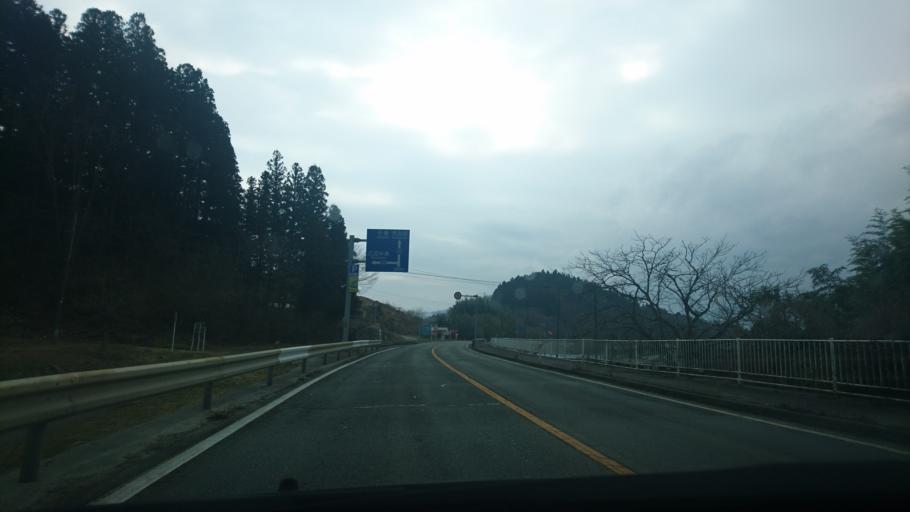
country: JP
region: Iwate
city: Ofunato
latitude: 39.0177
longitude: 141.6702
